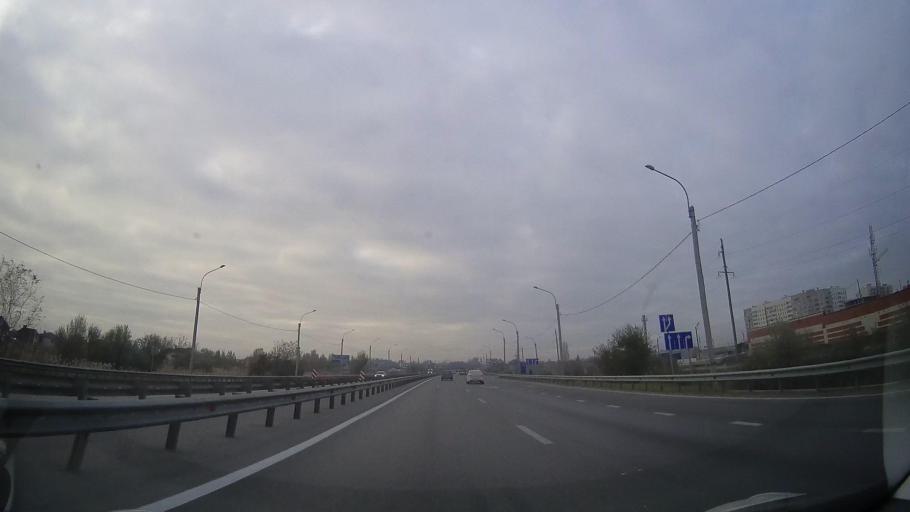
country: RU
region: Rostov
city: Bataysk
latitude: 47.1377
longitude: 39.7763
